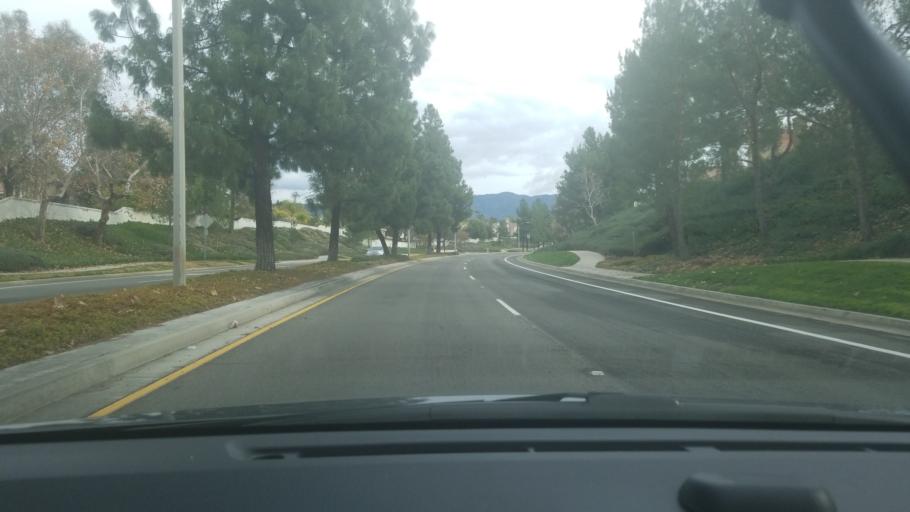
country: US
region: California
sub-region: Riverside County
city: Temecula
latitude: 33.4781
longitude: -117.0798
